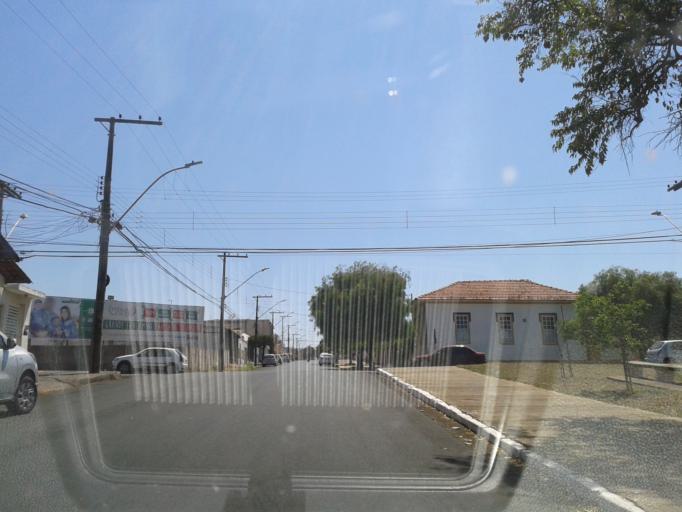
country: BR
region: Minas Gerais
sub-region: Araguari
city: Araguari
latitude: -18.6433
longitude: -48.1880
